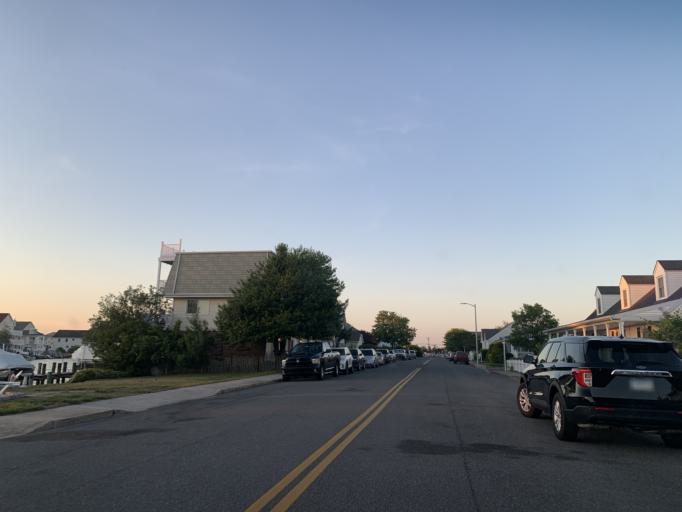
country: US
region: Delaware
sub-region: Sussex County
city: Bethany Beach
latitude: 38.4497
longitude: -75.0656
